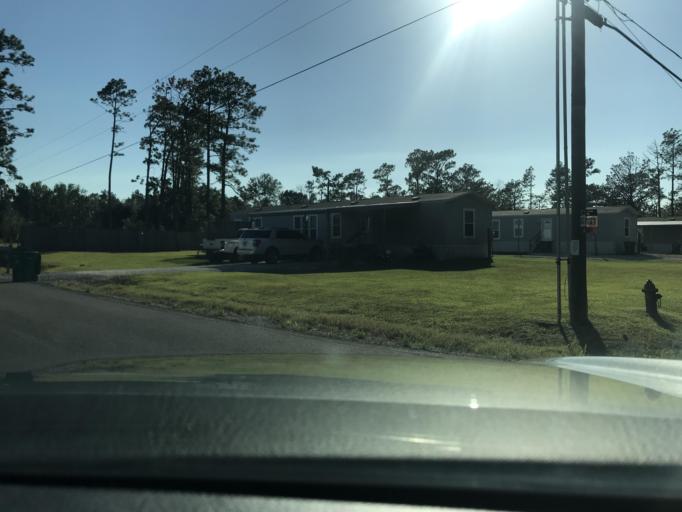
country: US
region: Louisiana
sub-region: Calcasieu Parish
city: Westlake
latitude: 30.3225
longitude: -93.2728
